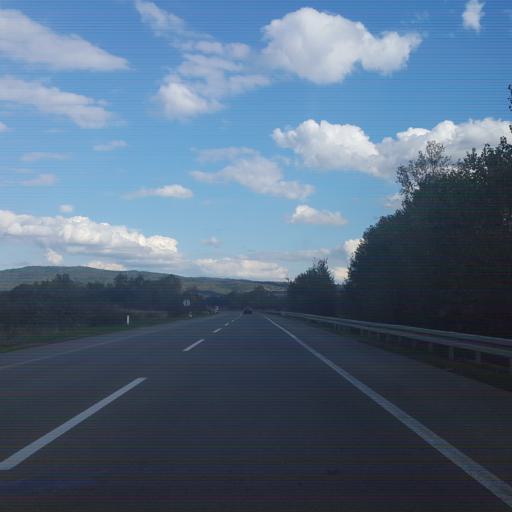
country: RS
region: Central Serbia
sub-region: Rasinski Okrug
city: Krusevac
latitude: 43.6093
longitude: 21.3307
